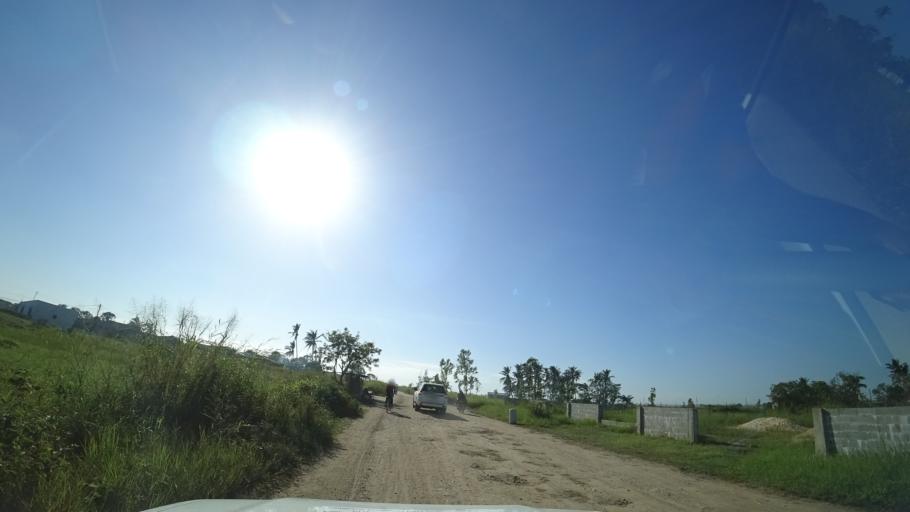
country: MZ
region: Sofala
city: Beira
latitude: -19.7643
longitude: 34.8988
